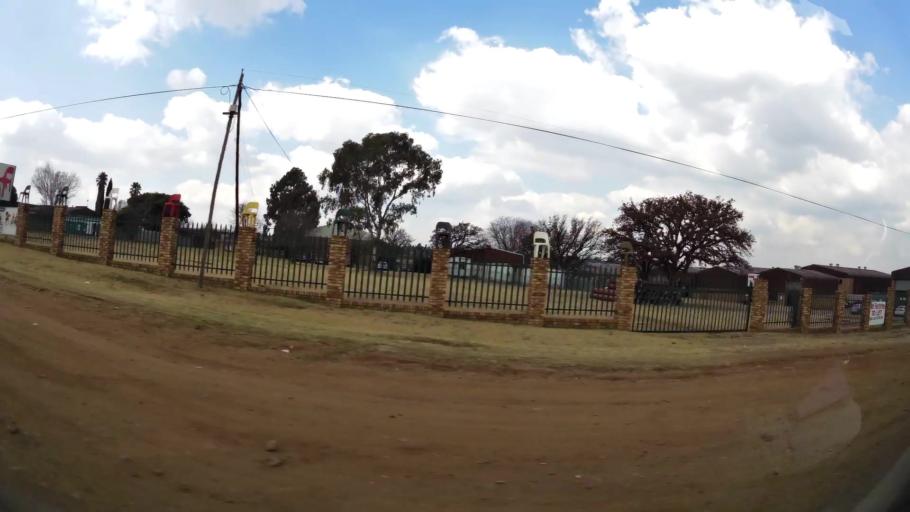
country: ZA
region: Gauteng
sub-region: Ekurhuleni Metropolitan Municipality
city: Benoni
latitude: -26.1316
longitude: 28.3530
